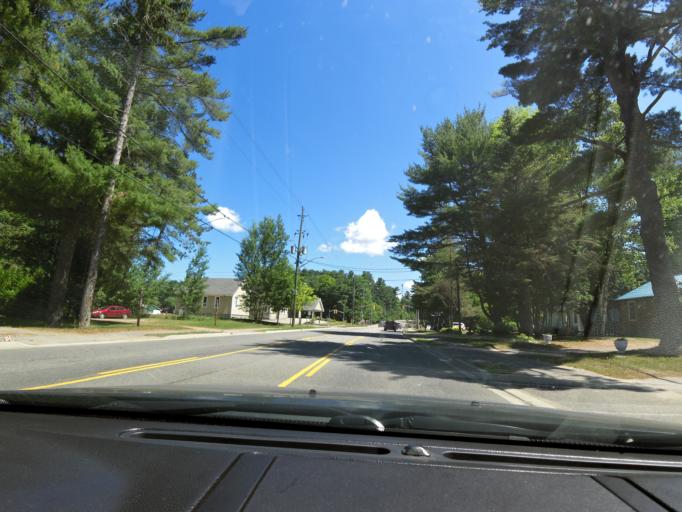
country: CA
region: Ontario
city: Bracebridge
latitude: 45.0482
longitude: -79.2989
